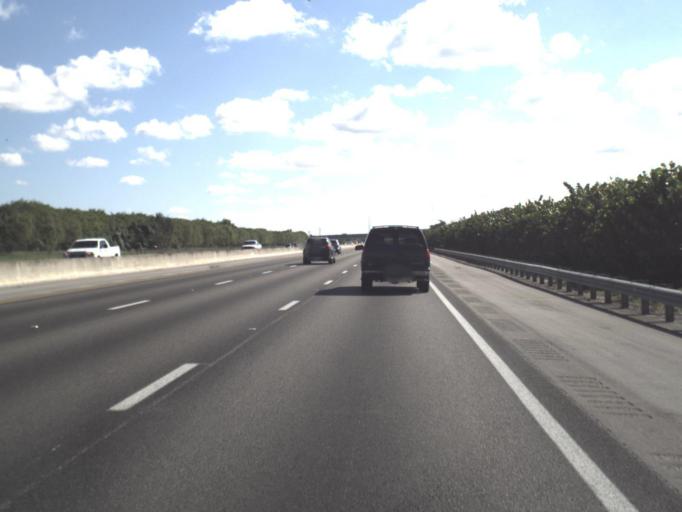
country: US
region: Florida
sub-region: Palm Beach County
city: Kings Point
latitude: 26.4024
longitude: -80.1714
